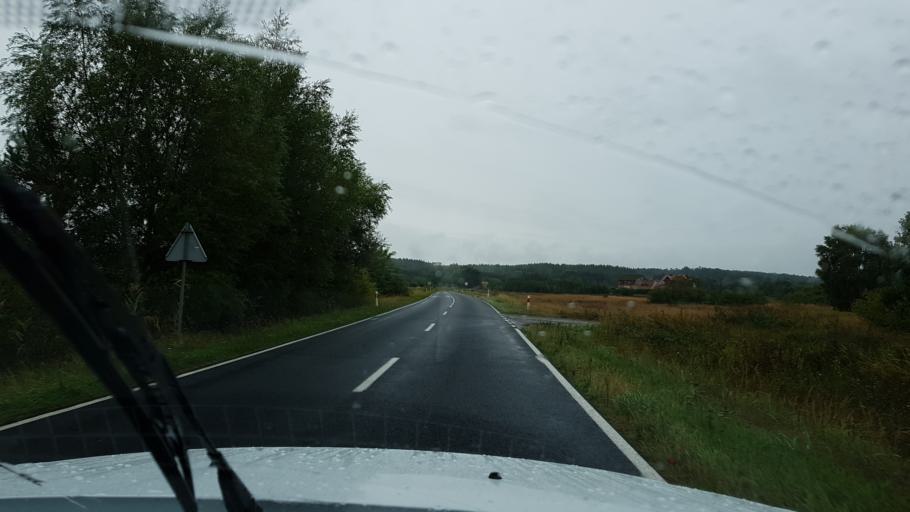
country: PL
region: West Pomeranian Voivodeship
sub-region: Powiat gryfinski
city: Widuchowa
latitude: 53.0788
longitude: 14.3749
